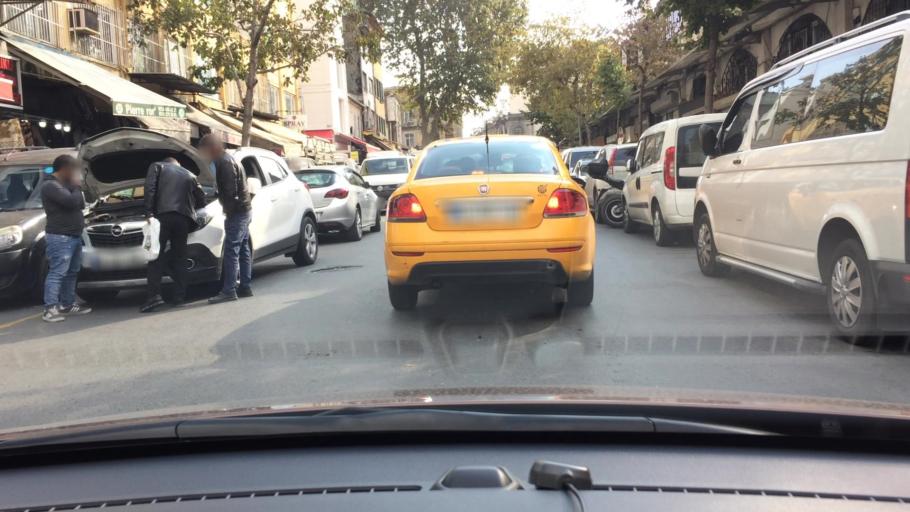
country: TR
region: Istanbul
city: Eminoenue
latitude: 41.0124
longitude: 28.9661
